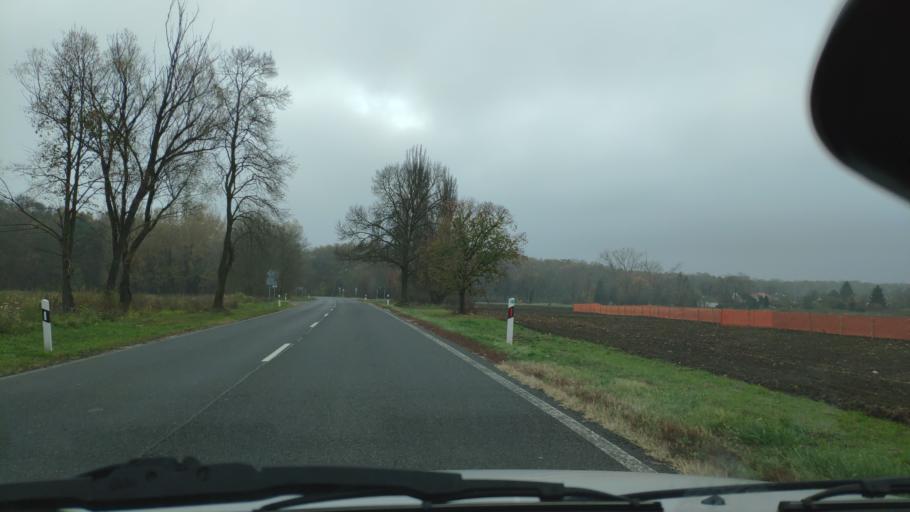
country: HU
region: Somogy
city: Balatonbereny
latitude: 46.6363
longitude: 17.2937
